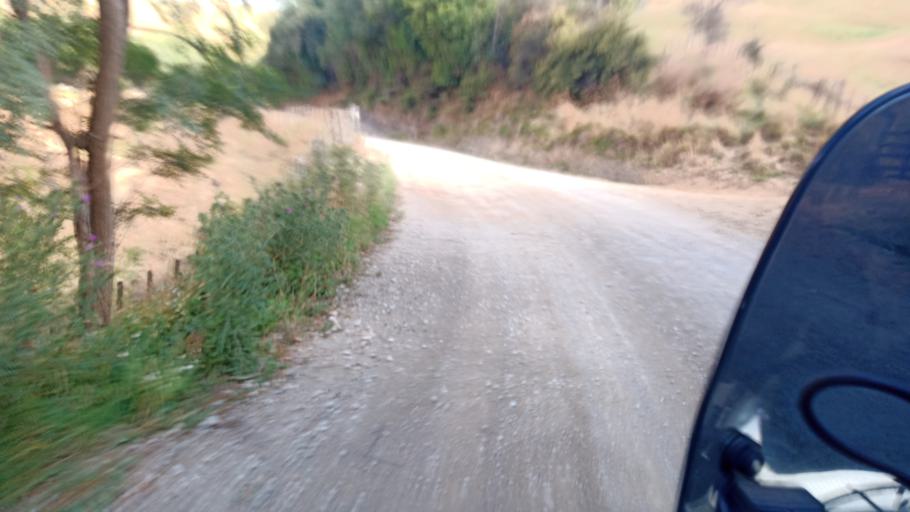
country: NZ
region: Hawke's Bay
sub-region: Wairoa District
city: Wairoa
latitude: -38.6076
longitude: 177.4602
